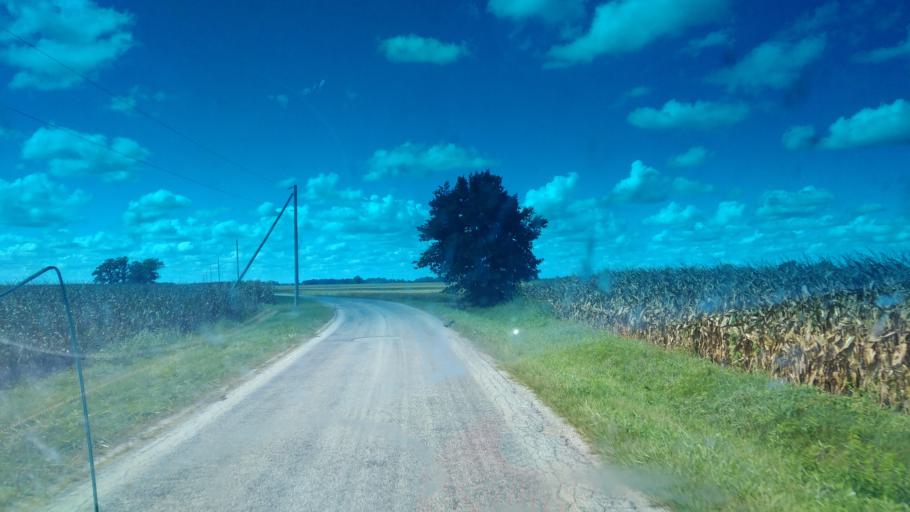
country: US
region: Ohio
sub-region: Madison County
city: Plain City
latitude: 40.0833
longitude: -83.3618
